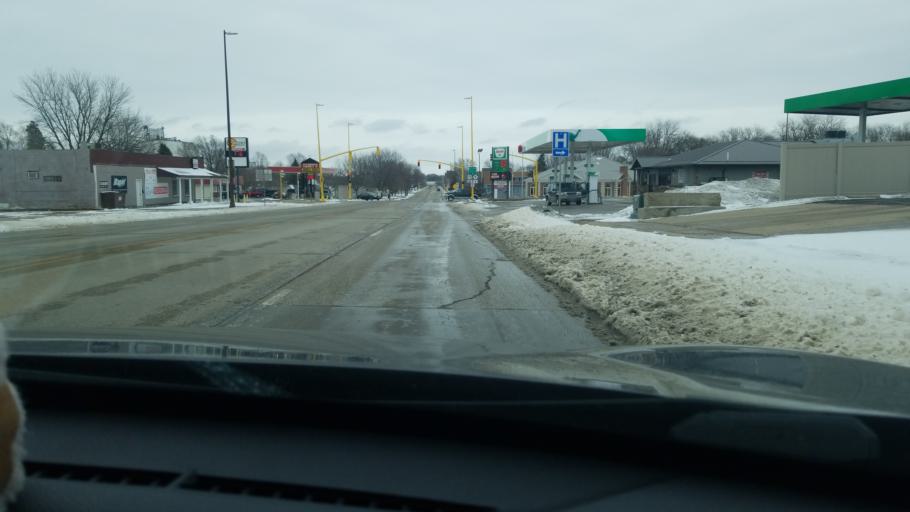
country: US
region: Iowa
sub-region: Lyon County
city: Rock Rapids
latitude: 43.4319
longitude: -96.1768
